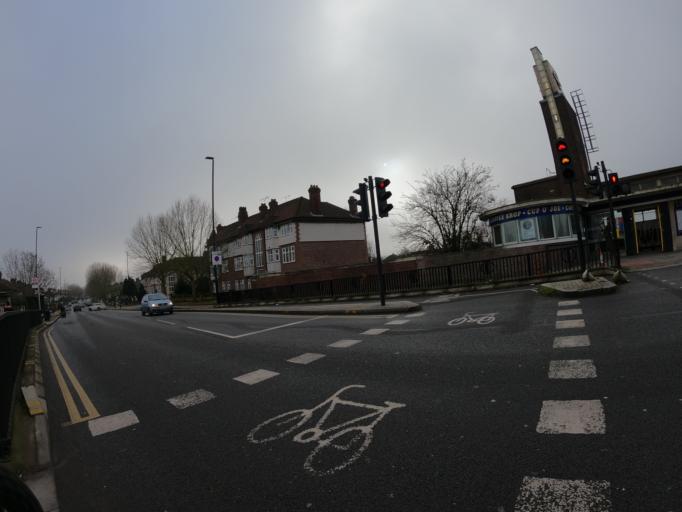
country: GB
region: England
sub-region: Greater London
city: Brentford
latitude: 51.4959
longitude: -0.3245
